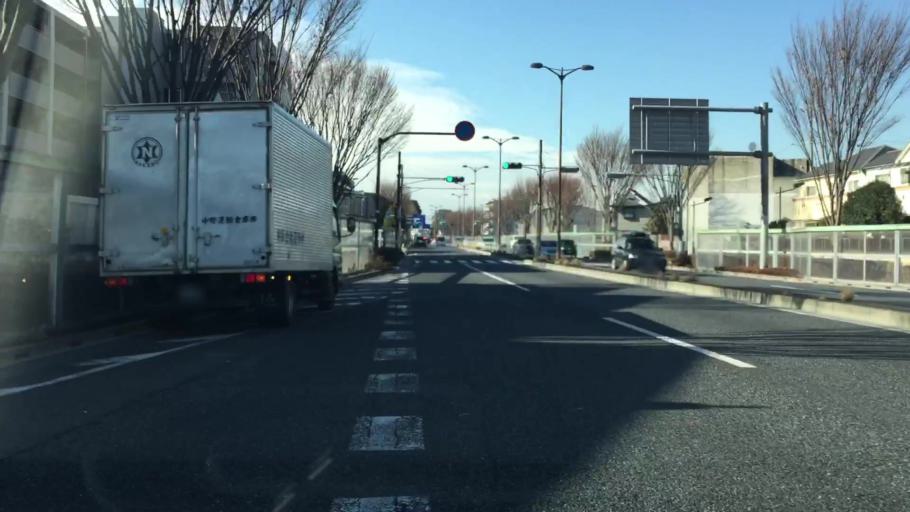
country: JP
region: Saitama
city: Wako
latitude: 35.7499
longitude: 139.6376
